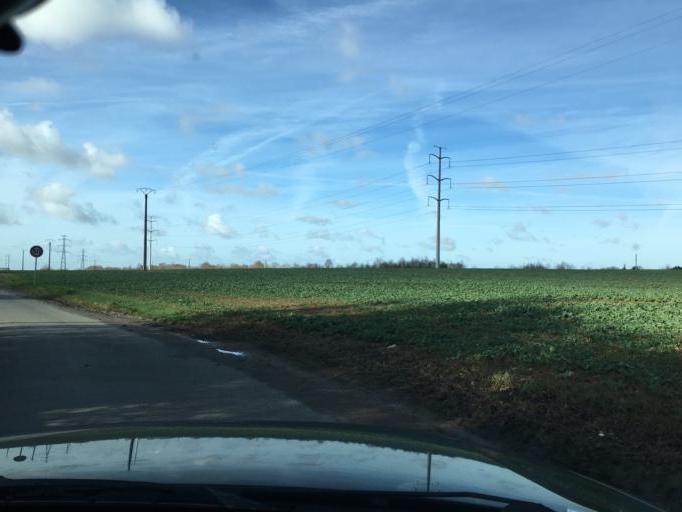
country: FR
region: Centre
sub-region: Departement du Loiret
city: Meung-sur-Loire
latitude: 47.8531
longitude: 1.6998
